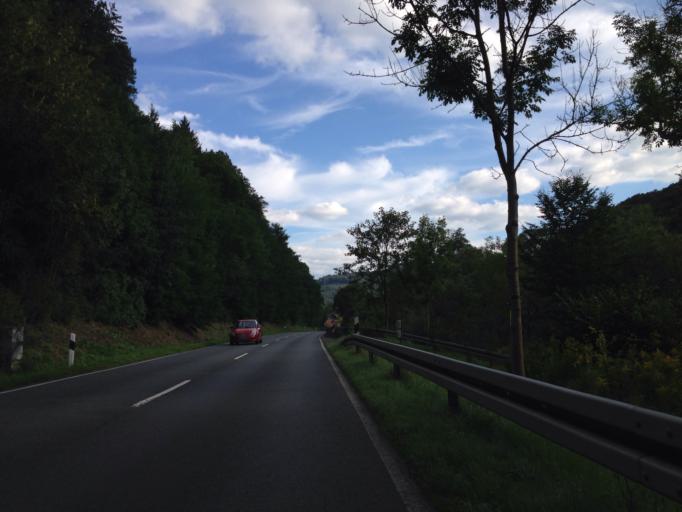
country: DE
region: Hesse
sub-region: Regierungsbezirk Giessen
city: Biedenkopf
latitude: 50.9251
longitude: 8.5010
